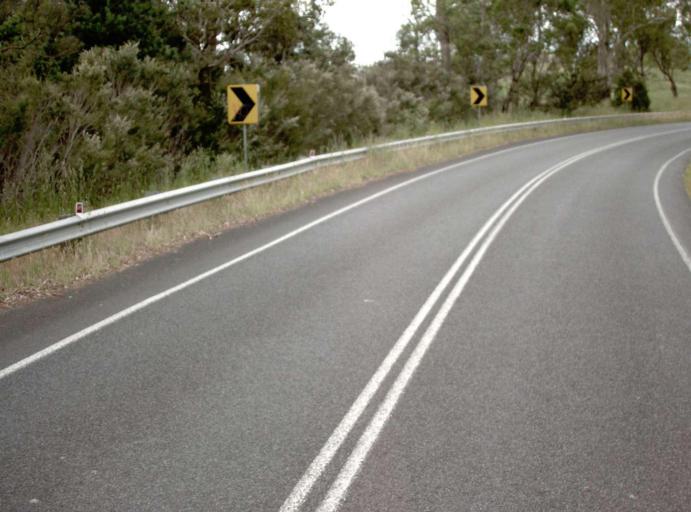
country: AU
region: Victoria
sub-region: Latrobe
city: Moe
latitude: -38.1365
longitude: 146.2598
